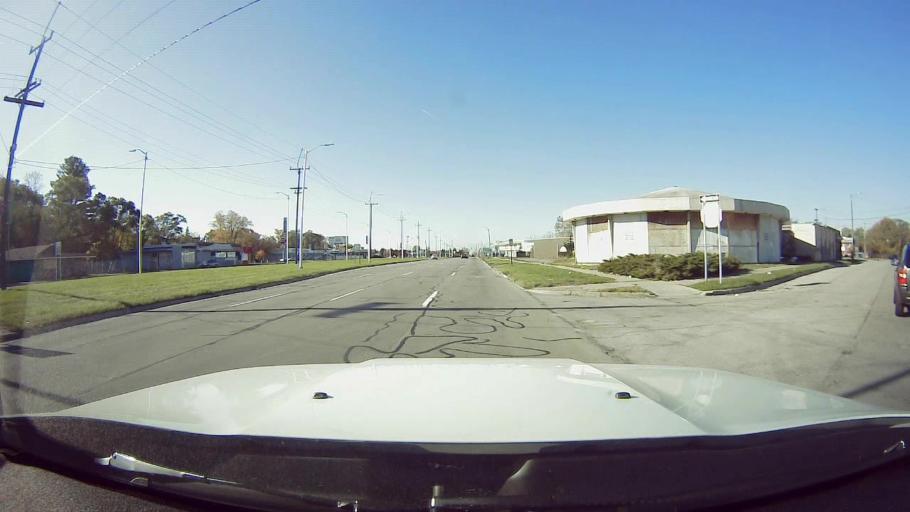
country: US
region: Michigan
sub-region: Wayne County
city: Redford
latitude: 42.4274
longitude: -83.2840
